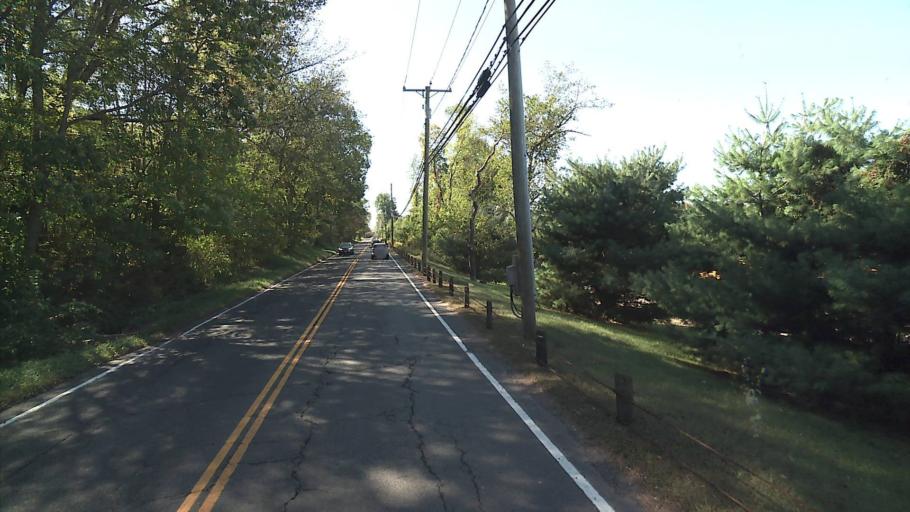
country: US
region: Connecticut
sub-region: Tolland County
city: Ellington
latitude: 41.9365
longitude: -72.4530
